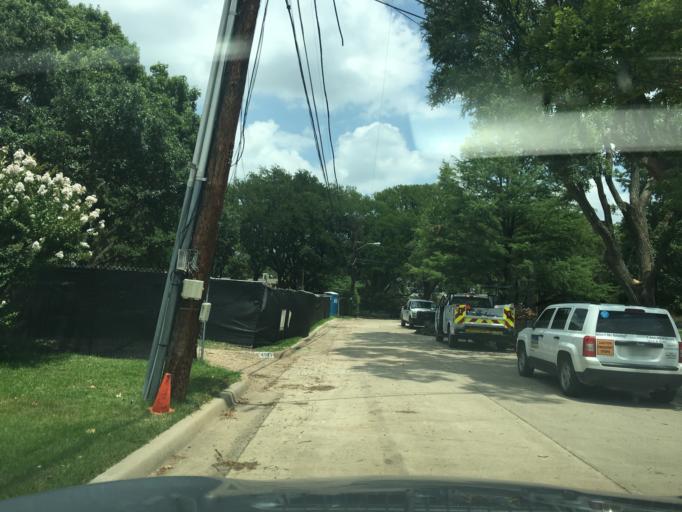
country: US
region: Texas
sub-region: Dallas County
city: University Park
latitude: 32.9001
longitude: -96.8244
